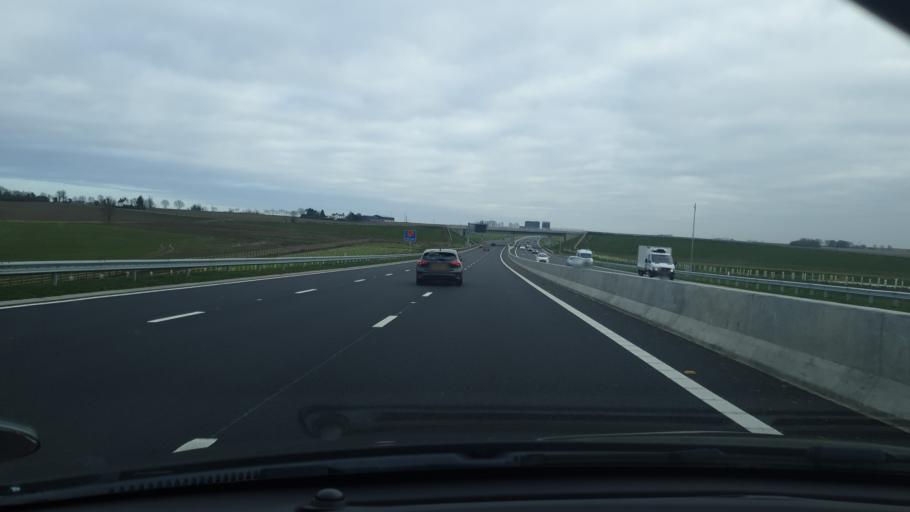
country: GB
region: England
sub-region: Cambridgeshire
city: Brampton
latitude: 52.2993
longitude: -0.2077
